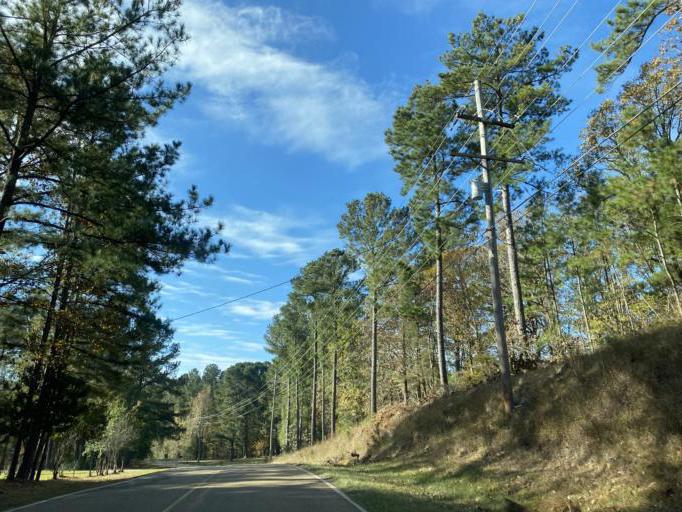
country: US
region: Mississippi
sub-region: Madison County
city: Ridgeland
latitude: 32.4655
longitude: -90.1843
